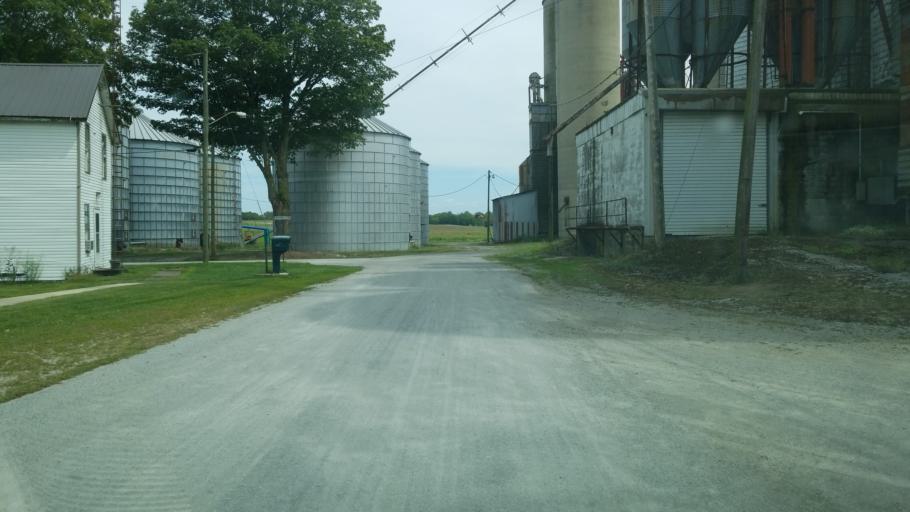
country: US
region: Ohio
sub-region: Hardin County
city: Kenton
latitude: 40.6186
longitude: -83.4675
